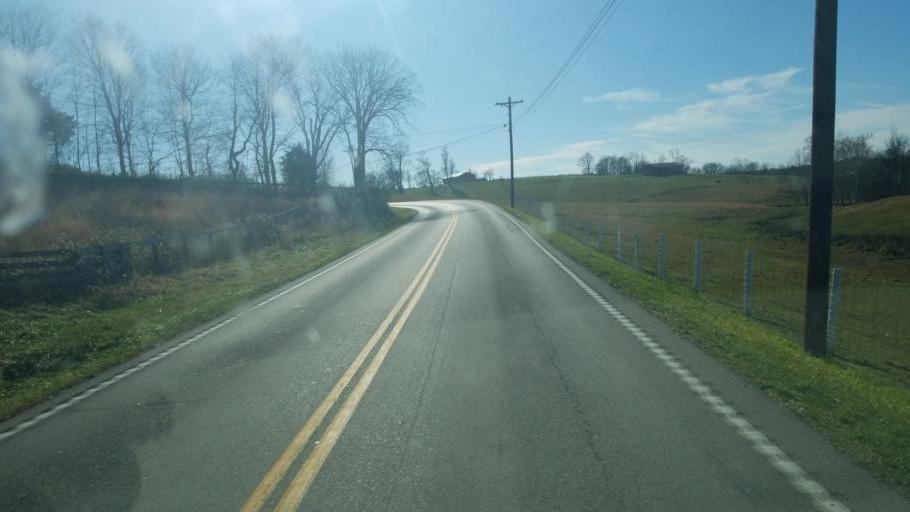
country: US
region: Kentucky
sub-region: Fleming County
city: Flemingsburg
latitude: 38.5151
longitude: -83.6203
